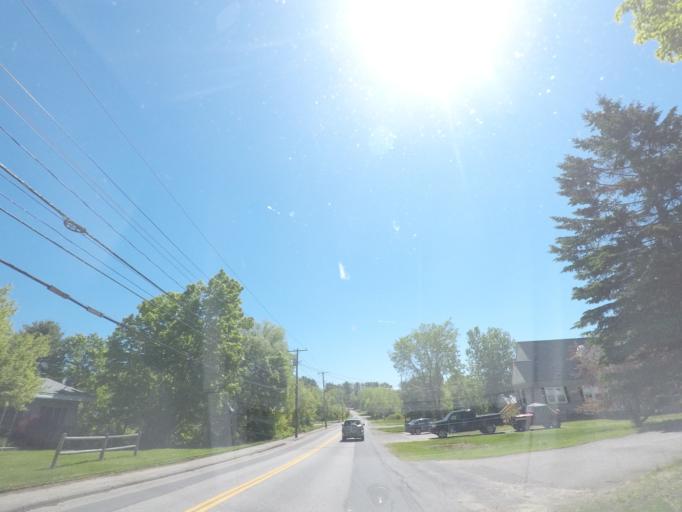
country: US
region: Maine
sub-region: Kennebec County
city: Augusta
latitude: 44.3188
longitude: -69.8055
